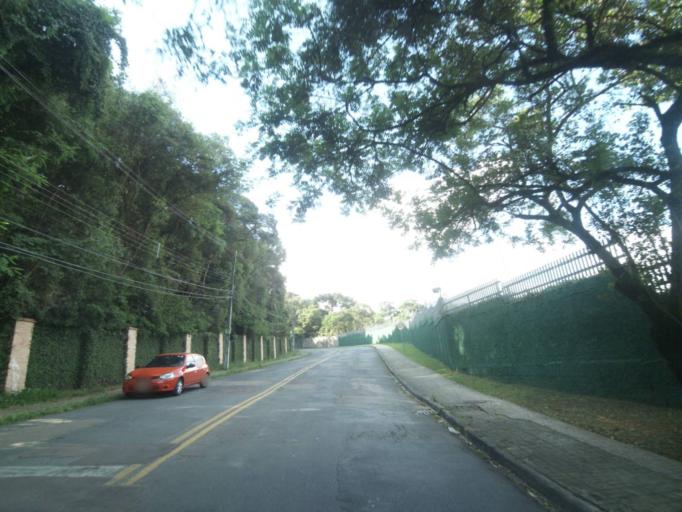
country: BR
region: Parana
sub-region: Curitiba
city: Curitiba
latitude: -25.3862
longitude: -49.3038
